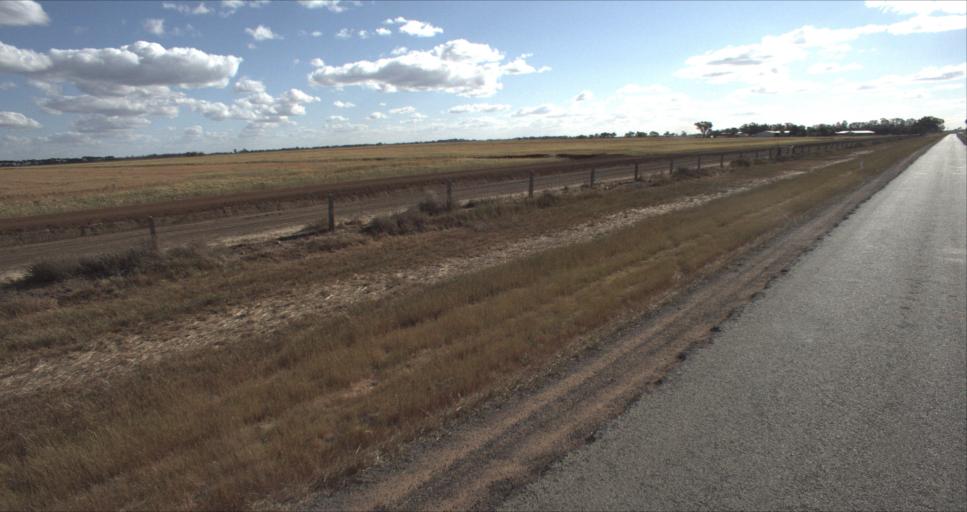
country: AU
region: New South Wales
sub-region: Leeton
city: Leeton
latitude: -34.4574
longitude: 146.2937
